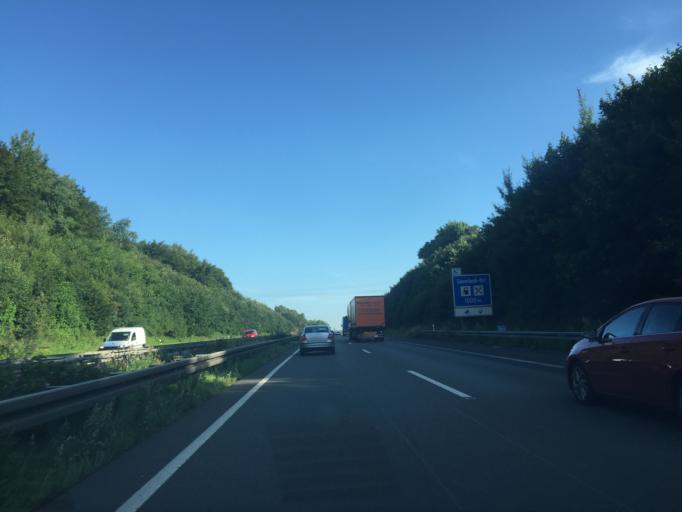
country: DE
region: North Rhine-Westphalia
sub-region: Regierungsbezirk Arnsberg
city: Luedenscheid
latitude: 51.2100
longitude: 7.6717
